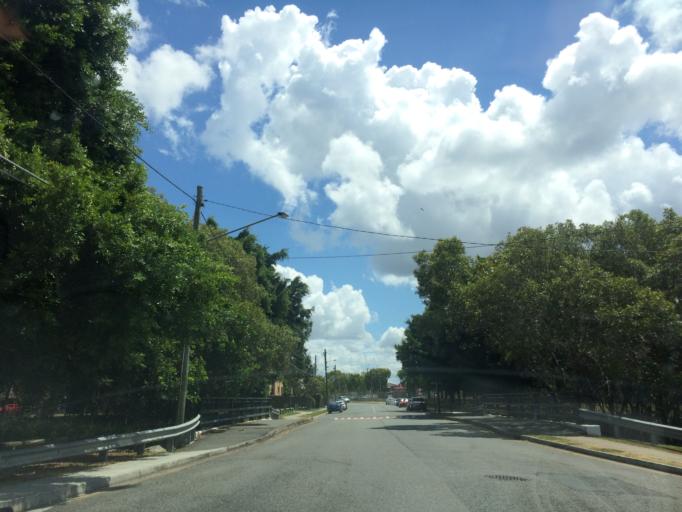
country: AU
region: Queensland
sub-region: Brisbane
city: Seven Hills
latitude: -27.4880
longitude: 153.0573
